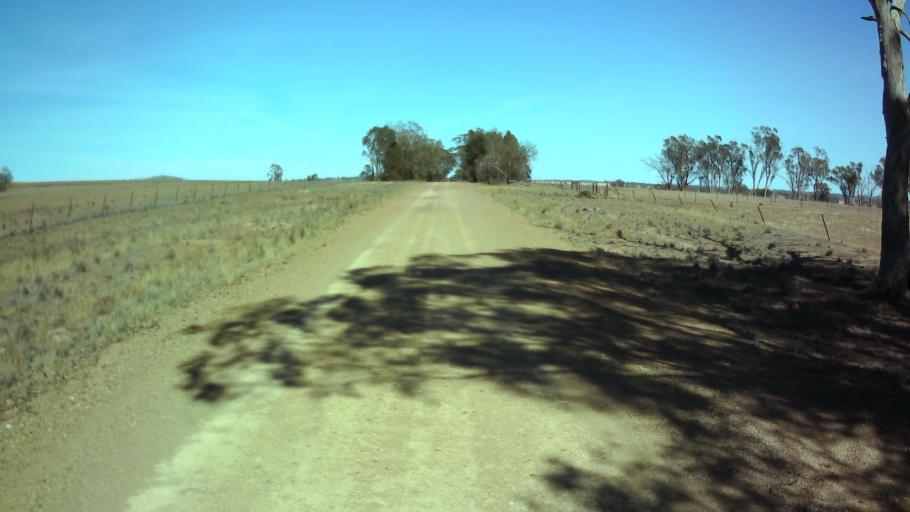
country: AU
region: New South Wales
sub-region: Weddin
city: Grenfell
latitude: -33.7526
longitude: 147.9120
